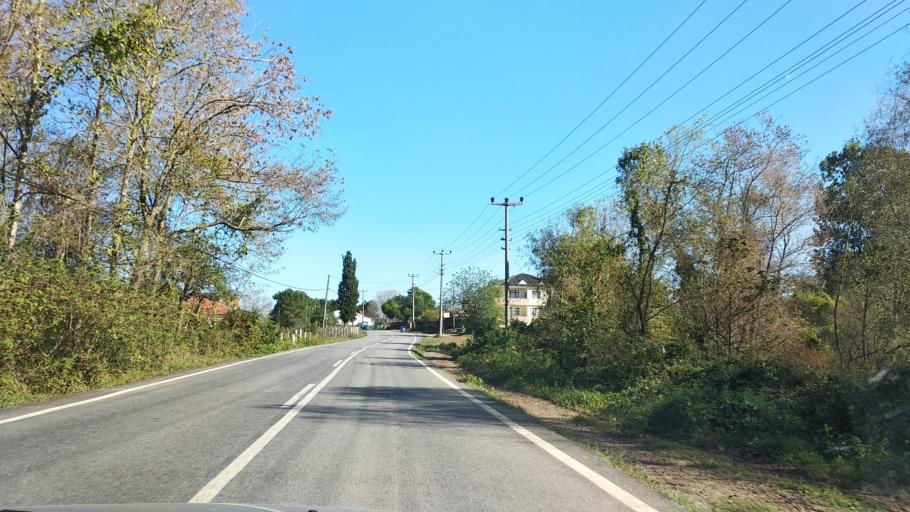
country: TR
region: Sakarya
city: Karasu
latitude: 41.1187
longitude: 30.6115
